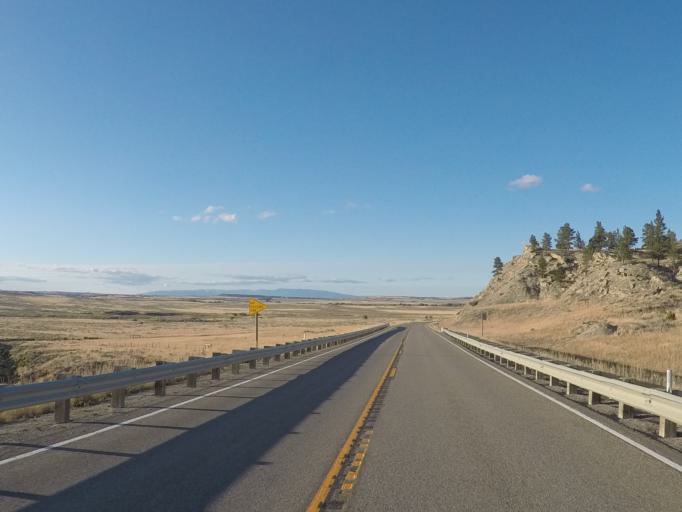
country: US
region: Montana
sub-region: Golden Valley County
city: Ryegate
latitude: 46.2691
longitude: -108.9392
